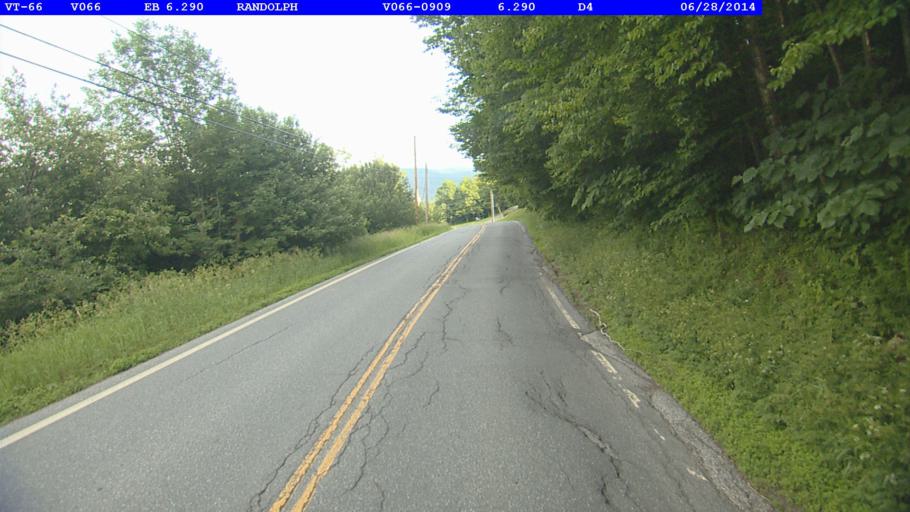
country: US
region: Vermont
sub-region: Orange County
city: Randolph
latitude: 43.9552
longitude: -72.5677
